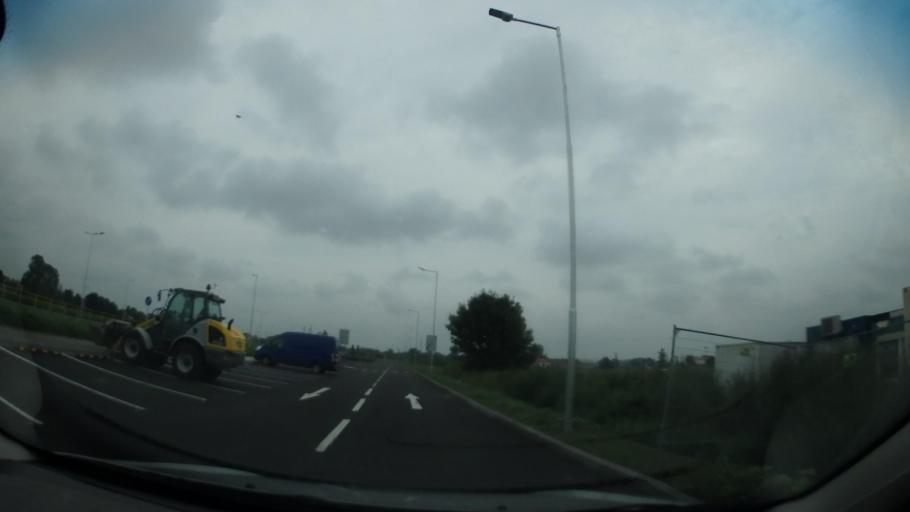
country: CZ
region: Olomoucky
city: Kojetin
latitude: 49.3391
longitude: 17.3102
